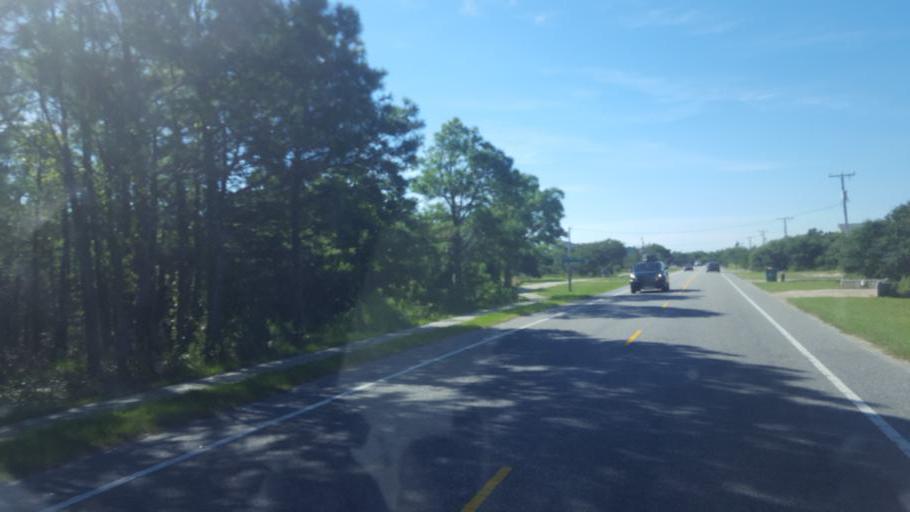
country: US
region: North Carolina
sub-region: Dare County
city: Southern Shores
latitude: 36.2904
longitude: -75.8013
